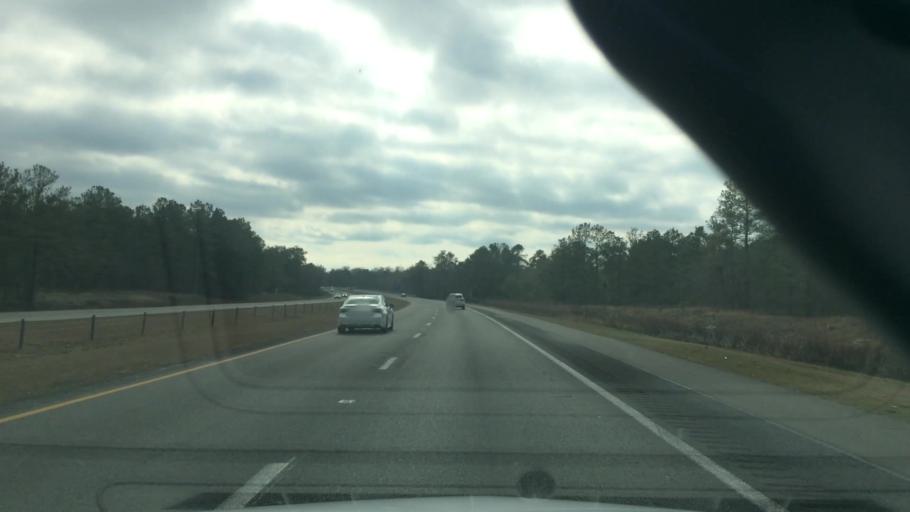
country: US
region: North Carolina
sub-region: New Hanover County
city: Castle Hayne
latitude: 34.3737
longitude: -77.8858
